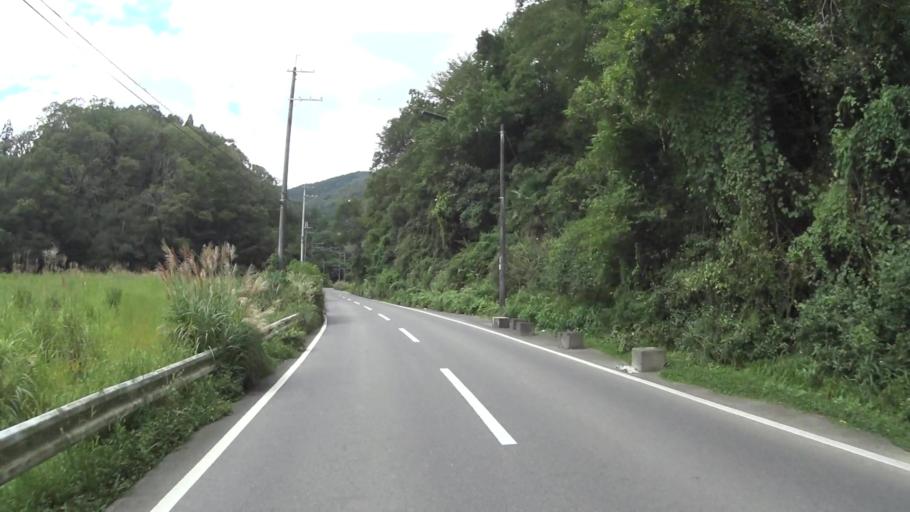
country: JP
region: Kyoto
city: Uji
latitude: 34.9176
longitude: 135.8858
